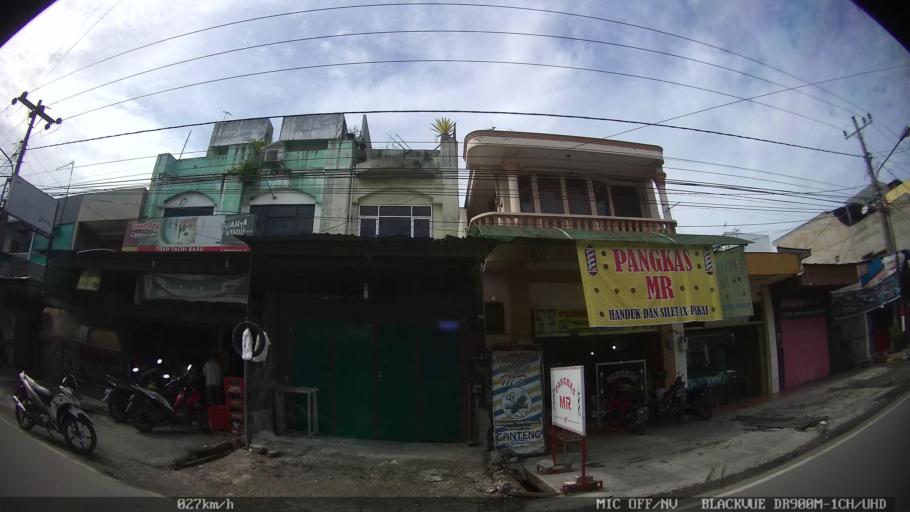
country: ID
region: North Sumatra
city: Medan
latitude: 3.6099
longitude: 98.6445
